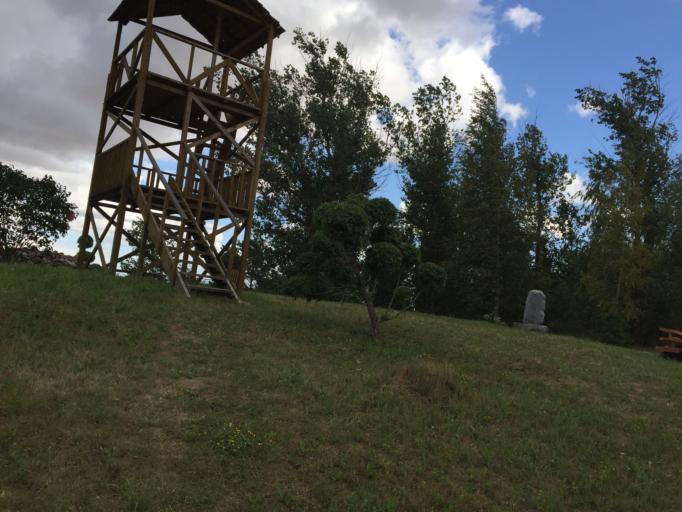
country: LT
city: Zagare
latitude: 56.3024
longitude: 23.3838
